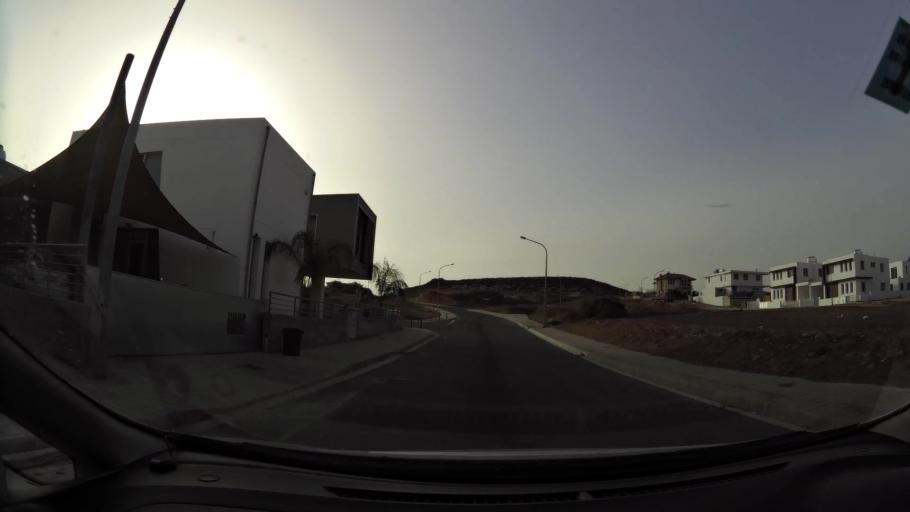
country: CY
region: Lefkosia
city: Geri
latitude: 35.0654
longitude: 33.3837
